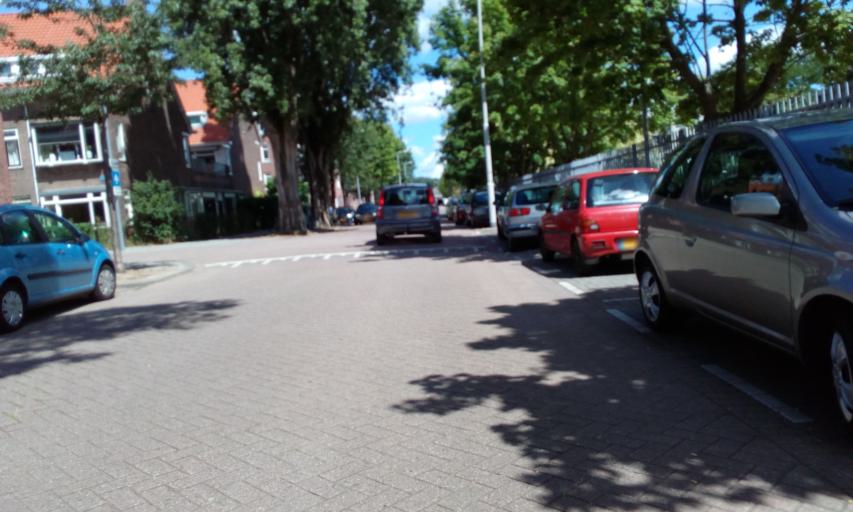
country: NL
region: South Holland
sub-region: Gemeente Rotterdam
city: Rotterdam
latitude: 51.9427
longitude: 4.4758
